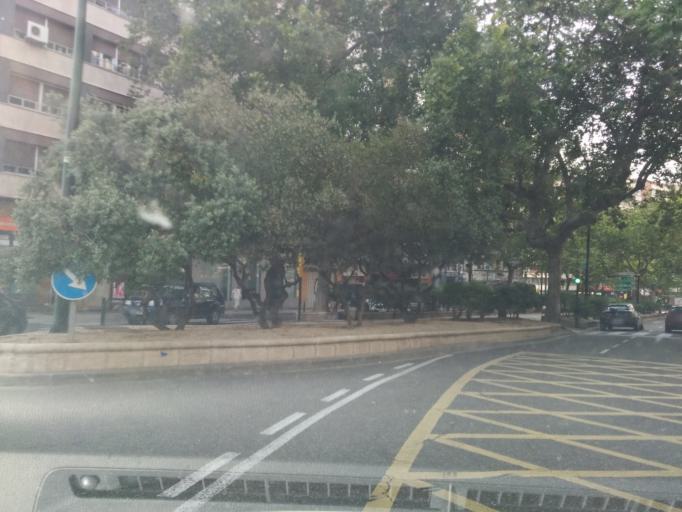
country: ES
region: Aragon
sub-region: Provincia de Zaragoza
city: Zaragoza
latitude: 41.6390
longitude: -0.8860
